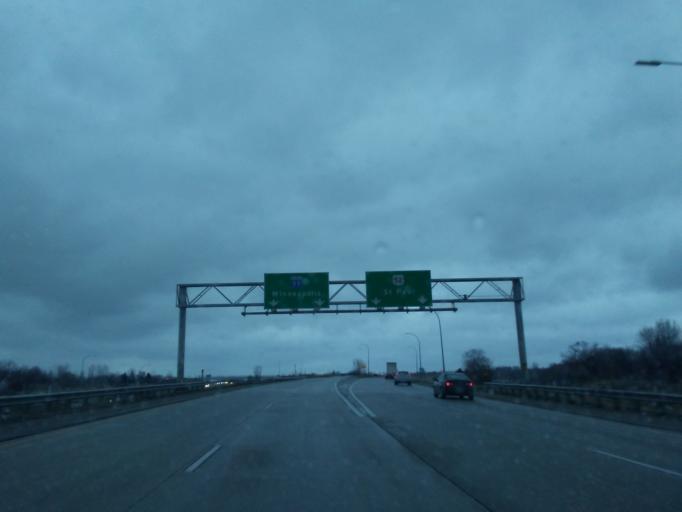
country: US
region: Minnesota
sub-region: Dakota County
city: Inver Grove Heights
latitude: 44.8209
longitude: -93.0530
